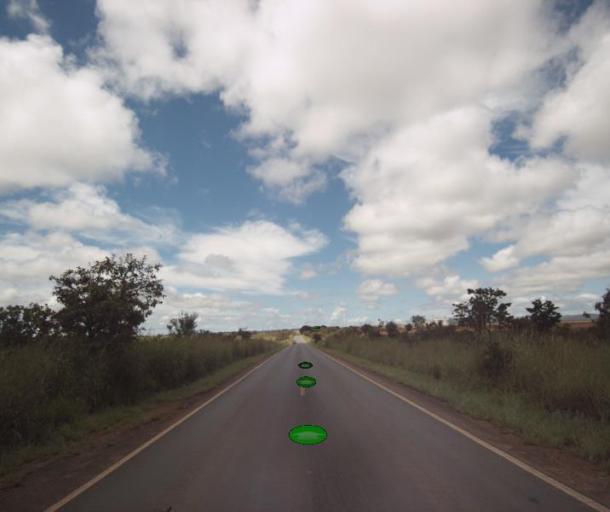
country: BR
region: Goias
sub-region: Padre Bernardo
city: Padre Bernardo
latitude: -15.2317
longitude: -48.2759
